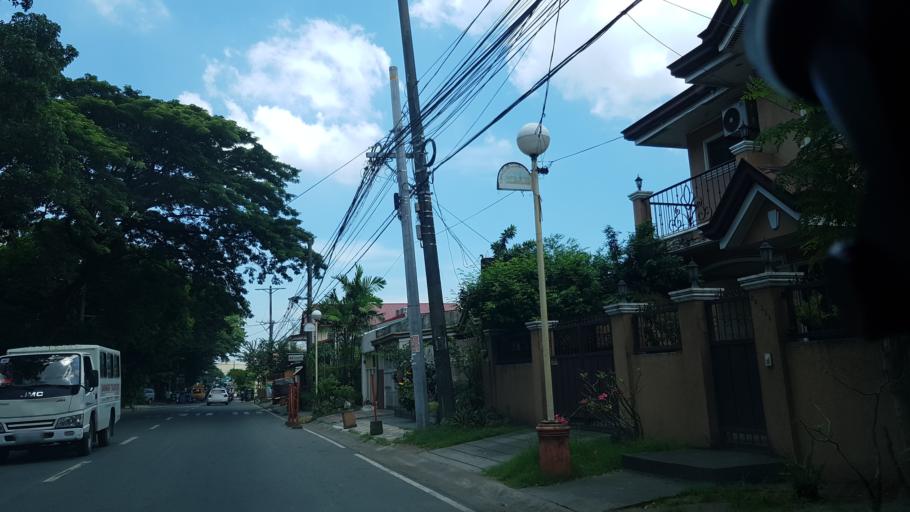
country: PH
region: Calabarzon
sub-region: Province of Rizal
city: Las Pinas
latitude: 14.4332
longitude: 120.9850
